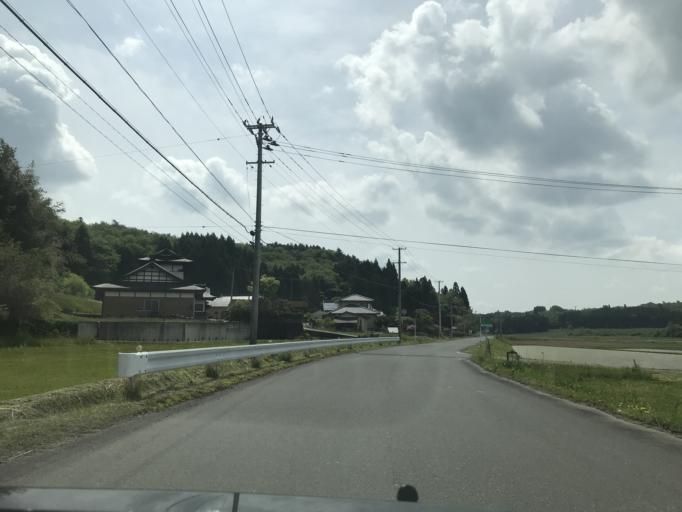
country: JP
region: Iwate
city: Ichinoseki
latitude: 38.8575
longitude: 141.0038
